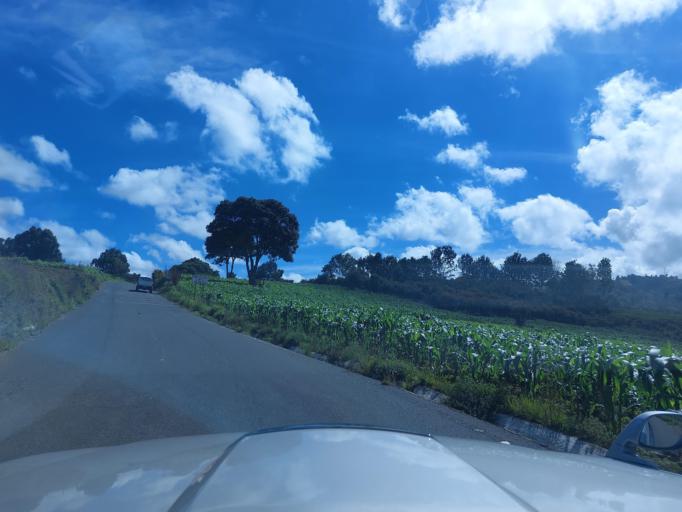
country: GT
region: Chimaltenango
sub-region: Municipio de Santa Cruz Balanya
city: Santa Cruz Balanya
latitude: 14.7089
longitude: -90.8954
